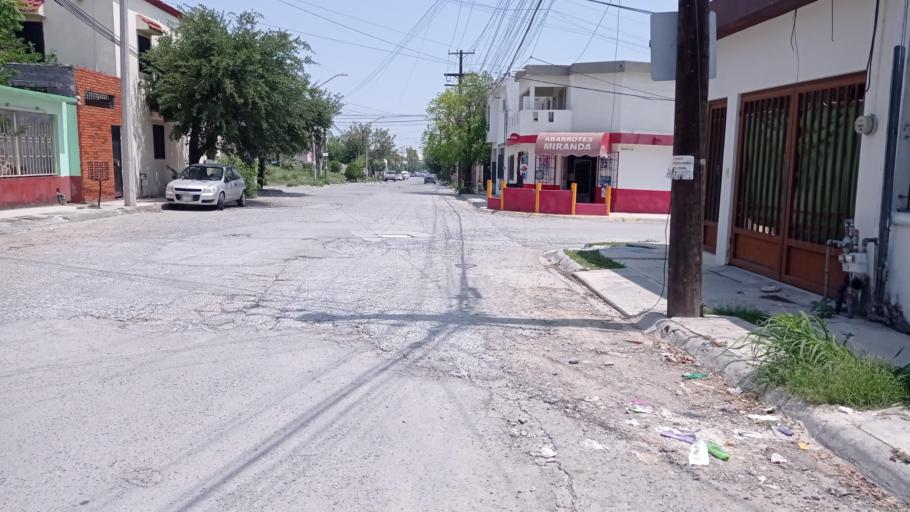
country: MX
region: Nuevo Leon
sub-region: Juarez
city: Jardines de la Silla (Jardines)
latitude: 25.6513
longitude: -100.1920
